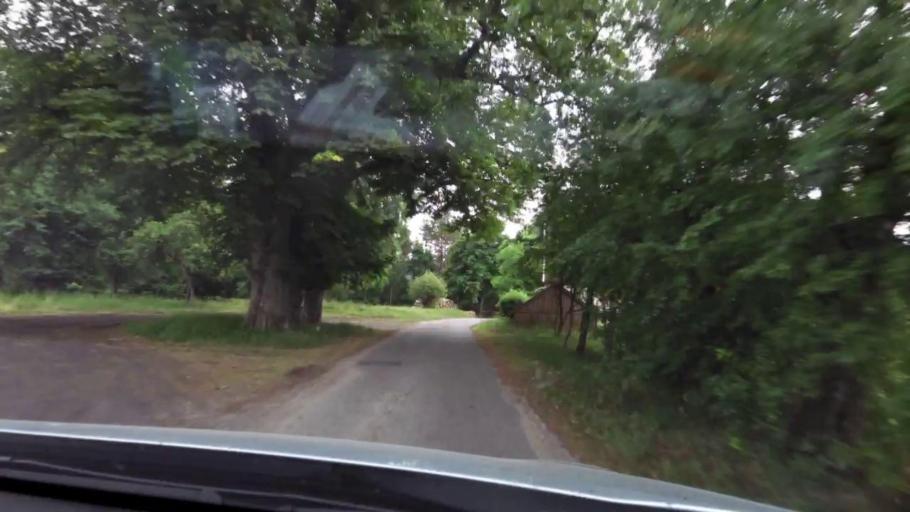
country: PL
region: Pomeranian Voivodeship
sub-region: Powiat bytowski
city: Trzebielino
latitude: 54.2319
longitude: 16.9999
